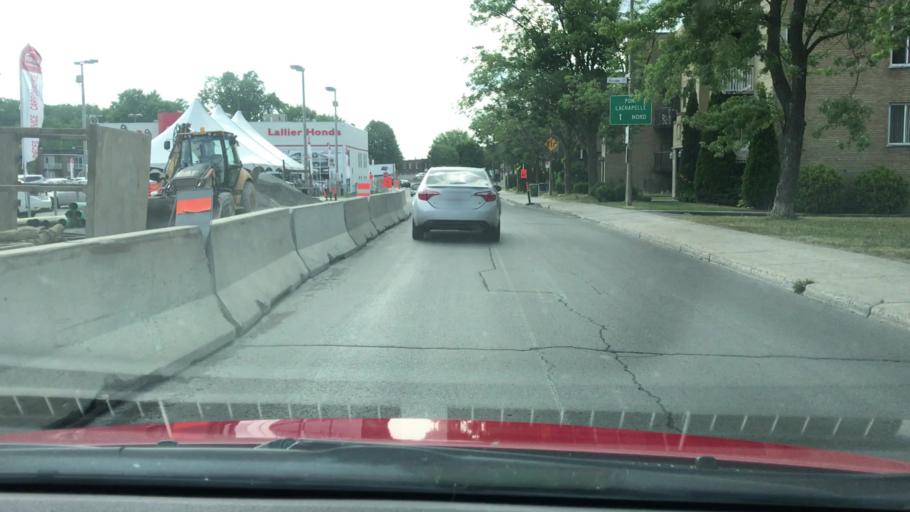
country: CA
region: Quebec
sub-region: Laval
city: Laval
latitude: 45.5315
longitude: -73.7235
